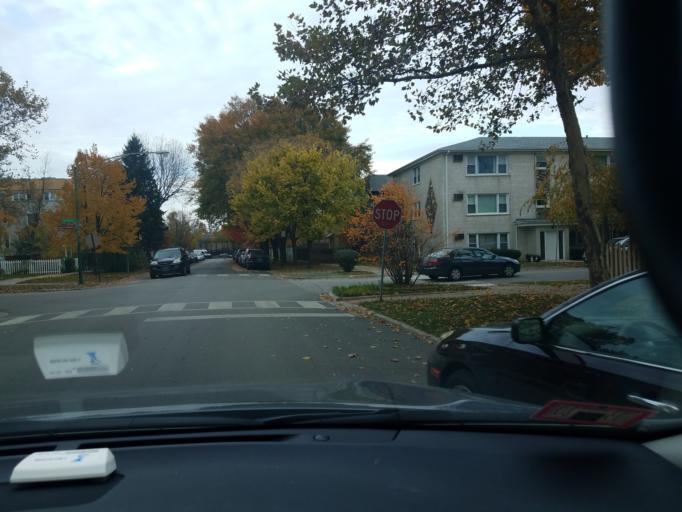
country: US
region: Illinois
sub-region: Cook County
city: Lincolnwood
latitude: 41.9516
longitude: -87.7308
